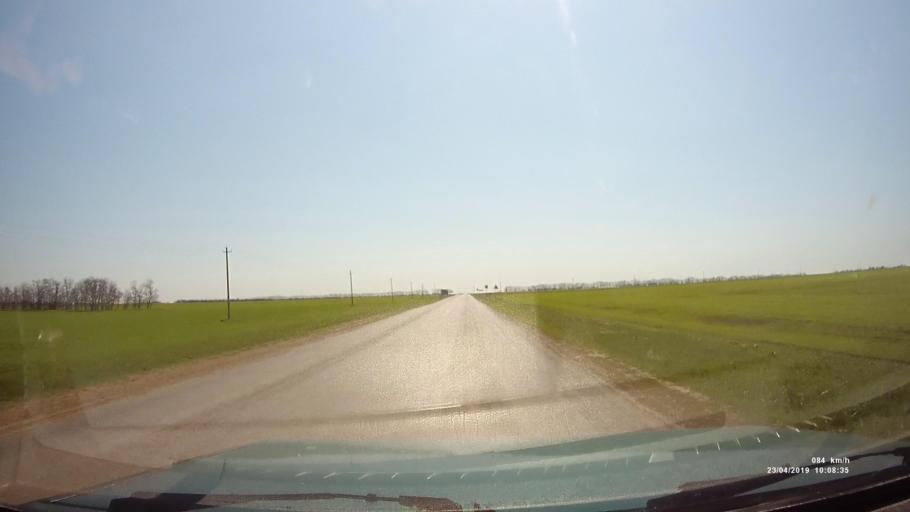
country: RU
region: Rostov
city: Sovetskoye
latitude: 46.7196
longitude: 42.2649
